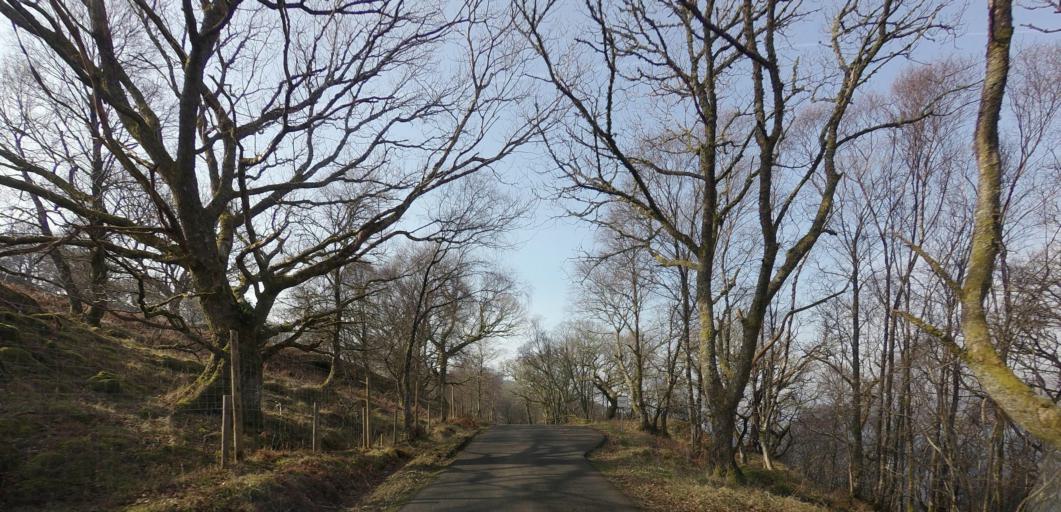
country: GB
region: Scotland
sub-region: Stirling
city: Callander
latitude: 56.4837
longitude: -4.2395
